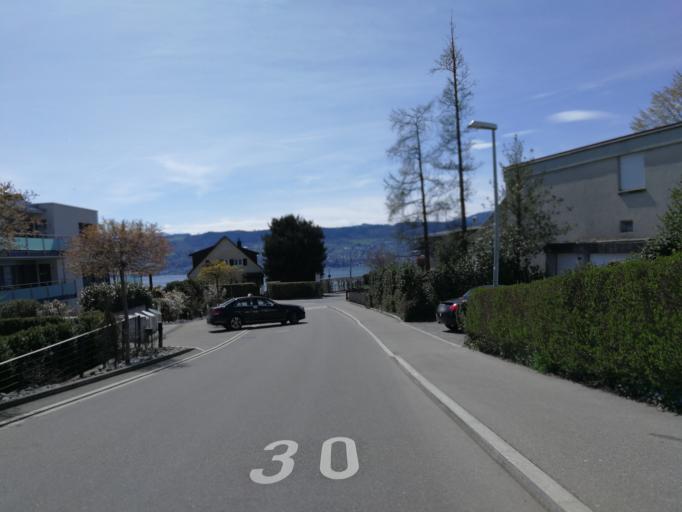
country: CH
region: Zurich
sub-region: Bezirk Meilen
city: Feldmeilen
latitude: 47.2798
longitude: 8.6243
